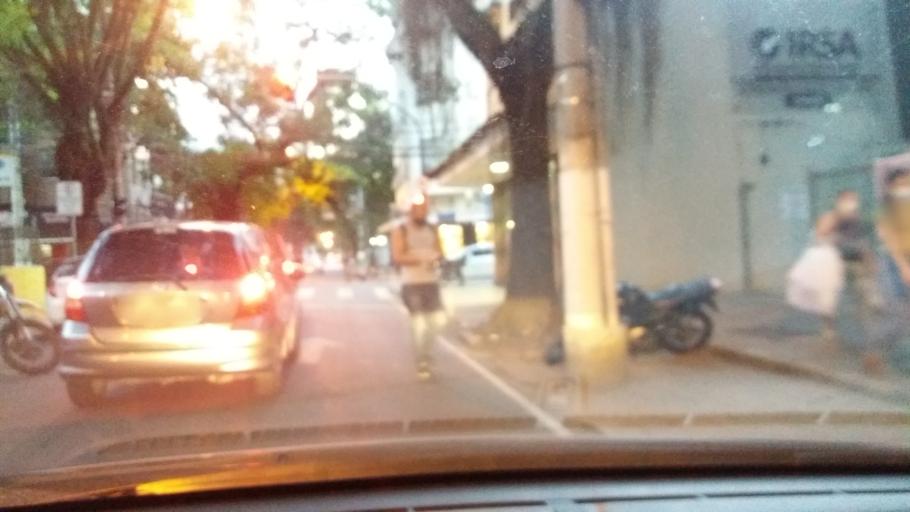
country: BR
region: Rio de Janeiro
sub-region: Niteroi
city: Niteroi
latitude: -22.9032
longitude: -43.1046
